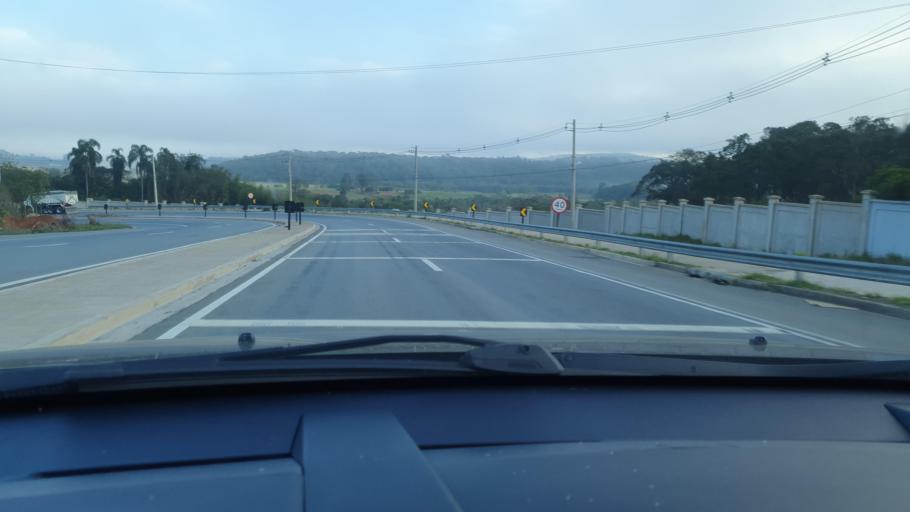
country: BR
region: Sao Paulo
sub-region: Vargem Grande Paulista
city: Vargem Grande Paulista
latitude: -23.6558
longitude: -47.0968
